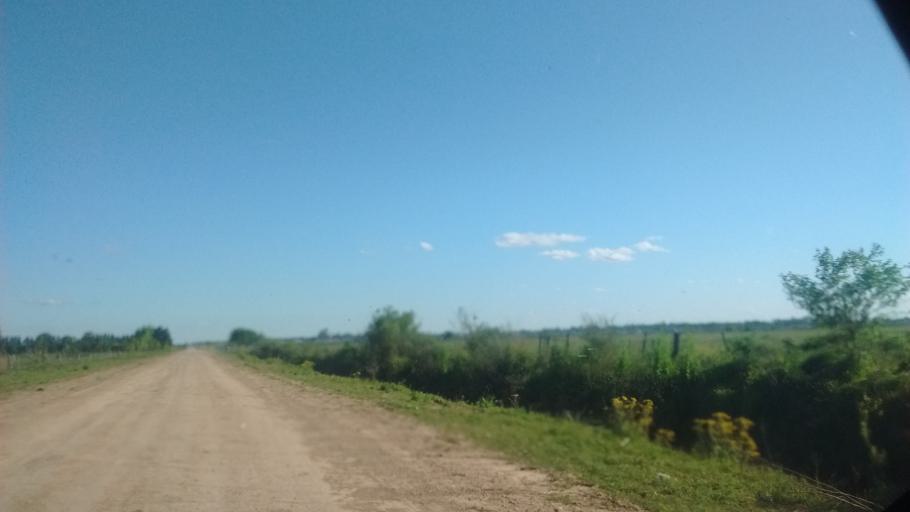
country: AR
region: Santa Fe
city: Funes
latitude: -32.8899
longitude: -60.7978
